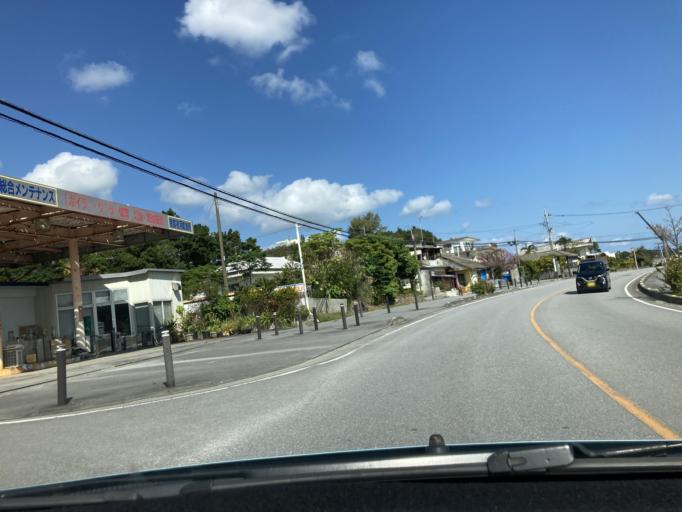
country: JP
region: Okinawa
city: Nago
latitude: 26.6187
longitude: 127.9988
